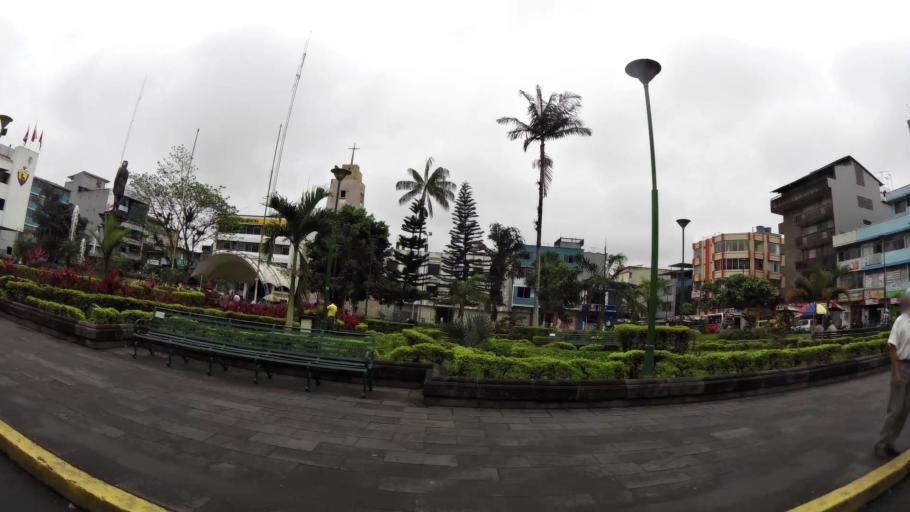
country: EC
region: Santo Domingo de los Tsachilas
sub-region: Canton Santo Domingo de los Colorados
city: Santo Domingo de los Colorados
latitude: -0.2550
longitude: -79.1685
